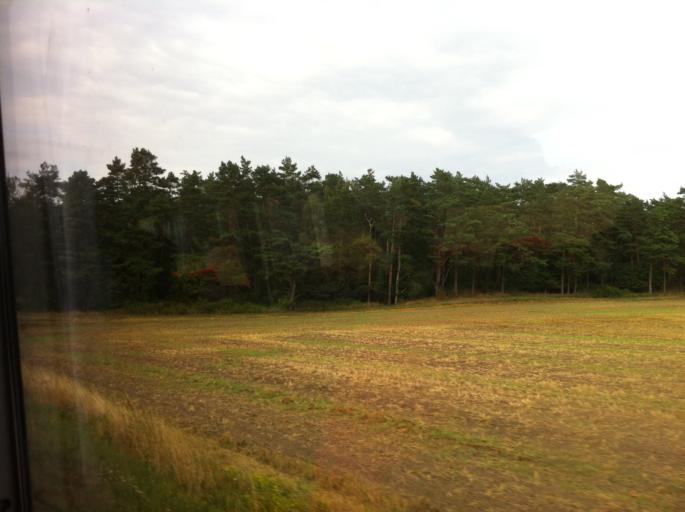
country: SE
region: Skane
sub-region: Kristianstads Kommun
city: Degeberga
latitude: 55.8491
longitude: 14.0960
